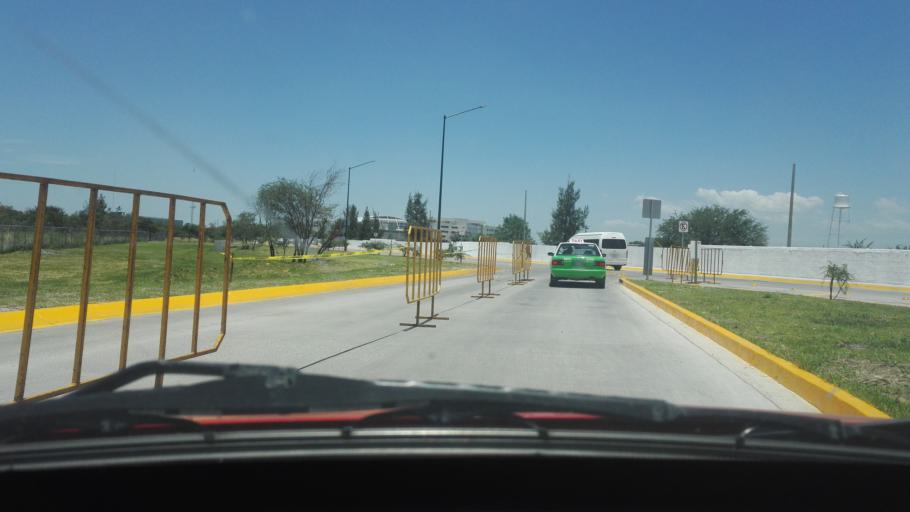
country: MX
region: Guanajuato
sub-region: Leon
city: Ladrilleras del Refugio
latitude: 21.0588
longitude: -101.5678
